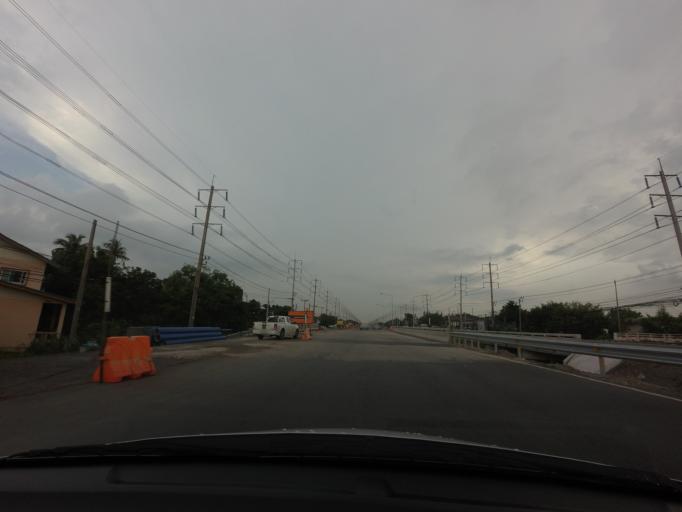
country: TH
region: Bangkok
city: Nong Chok
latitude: 13.8098
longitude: 100.8093
